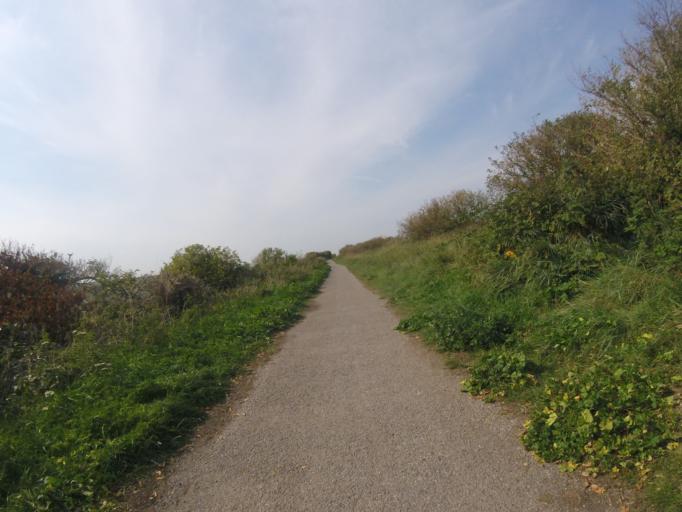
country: GB
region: England
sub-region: East Sussex
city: Portslade
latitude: 50.8580
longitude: -0.1988
